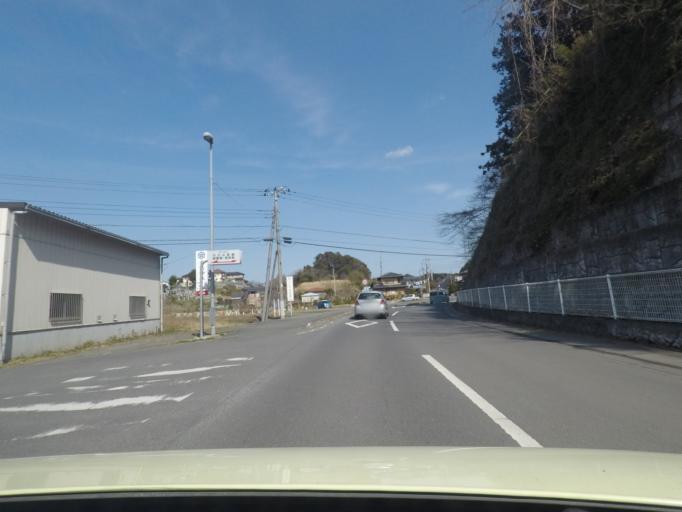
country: JP
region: Ibaraki
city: Ishioka
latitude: 36.1710
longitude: 140.3601
